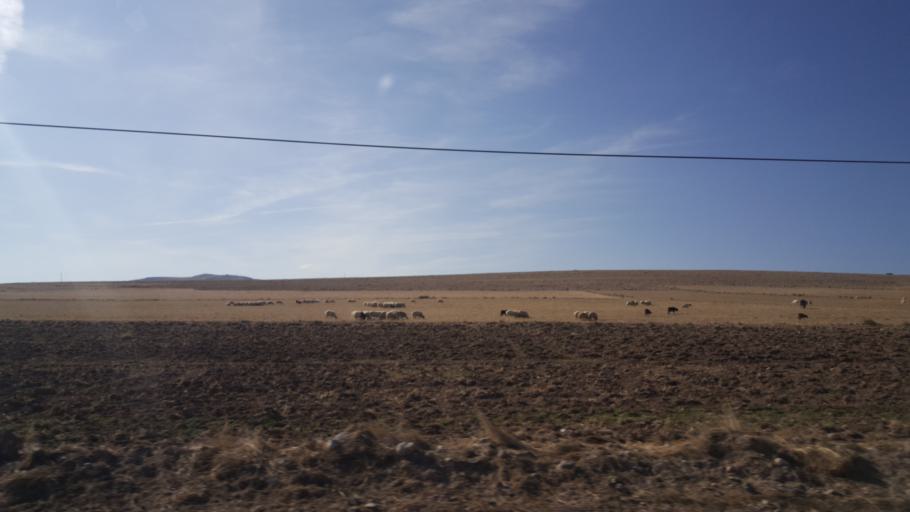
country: TR
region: Ankara
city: Altpinar
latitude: 39.2322
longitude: 32.7426
